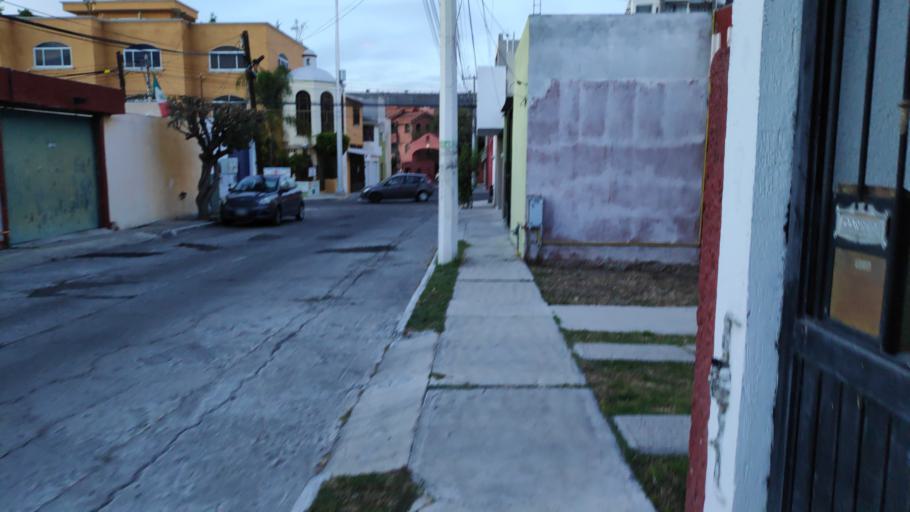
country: MX
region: Queretaro
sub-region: Queretaro
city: Santiago de Queretaro
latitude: 20.5820
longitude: -100.3810
